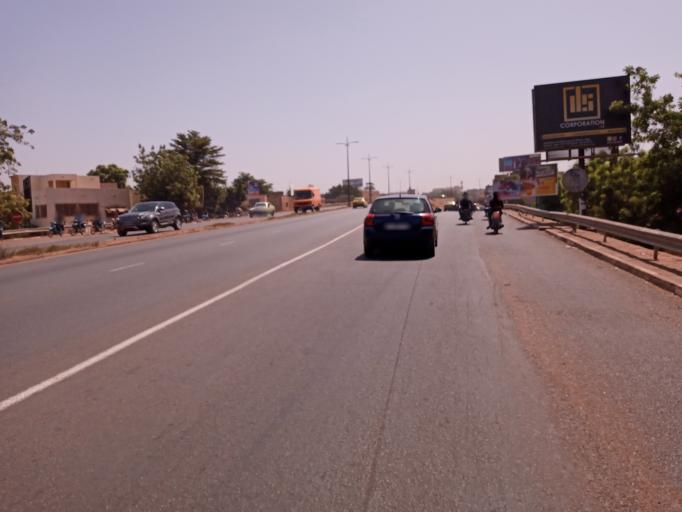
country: ML
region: Bamako
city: Bamako
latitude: 12.6161
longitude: -7.9998
